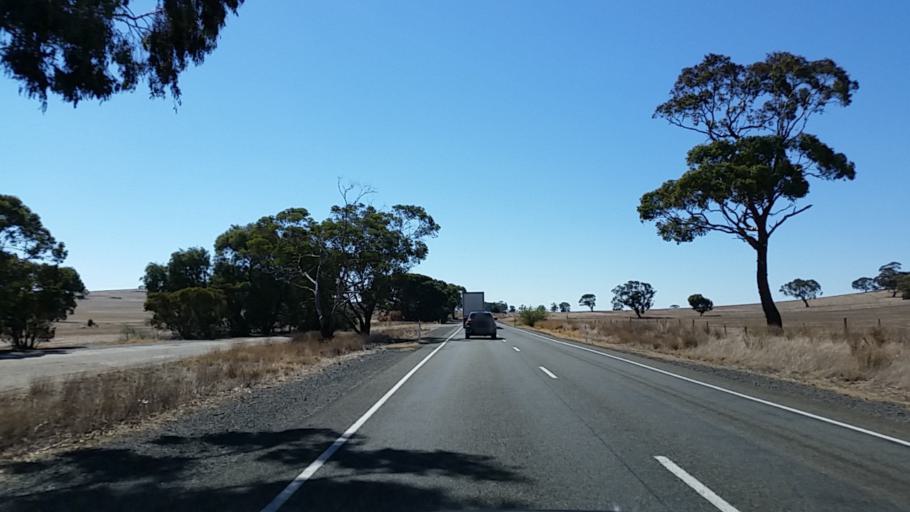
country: AU
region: South Australia
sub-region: Clare and Gilbert Valleys
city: Clare
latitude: -34.0479
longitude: 138.7979
